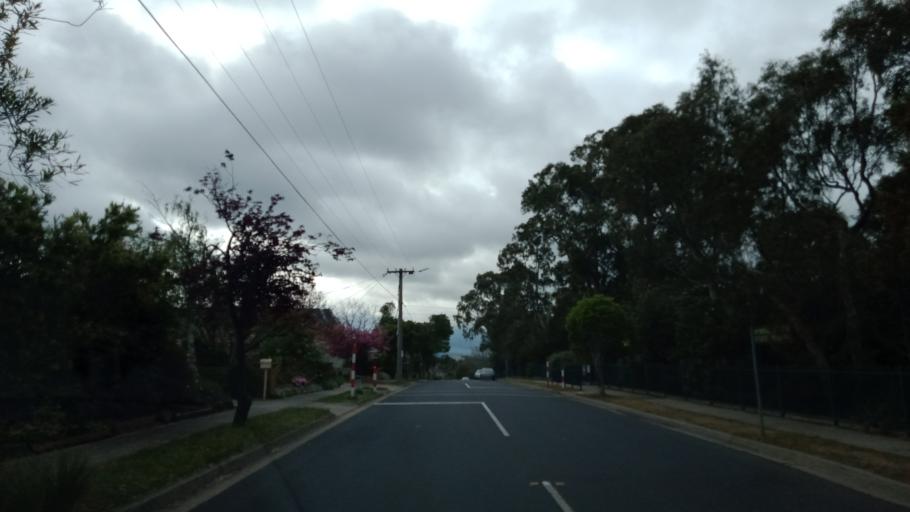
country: AU
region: Victoria
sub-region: Monash
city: Notting Hill
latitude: -37.8789
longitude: 145.1429
